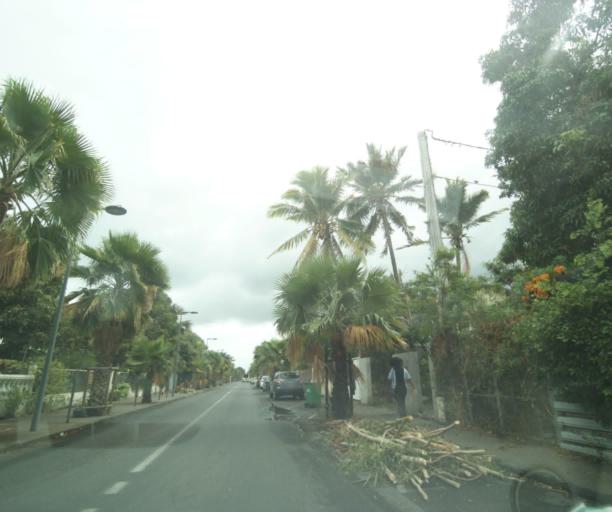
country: RE
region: Reunion
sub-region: Reunion
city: Saint-Paul
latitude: -20.9969
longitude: 55.2836
